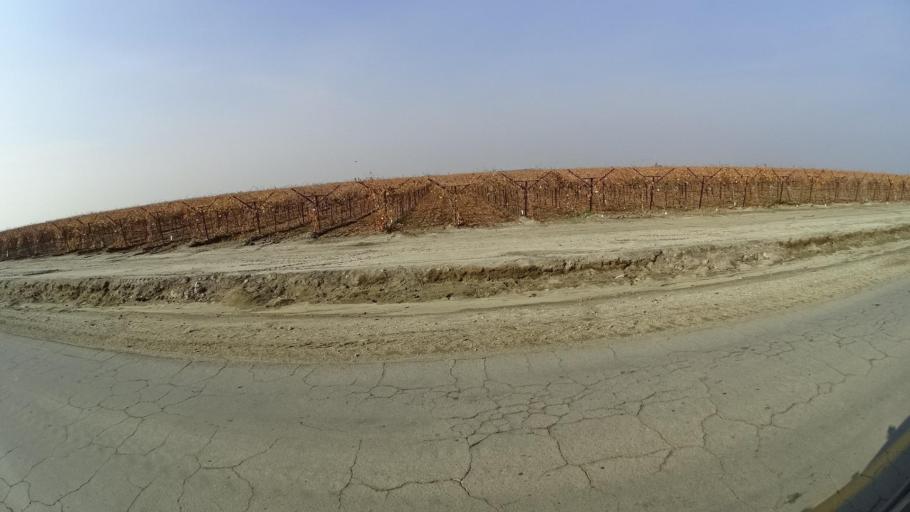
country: US
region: California
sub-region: Kern County
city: Arvin
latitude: 35.0862
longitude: -118.8465
